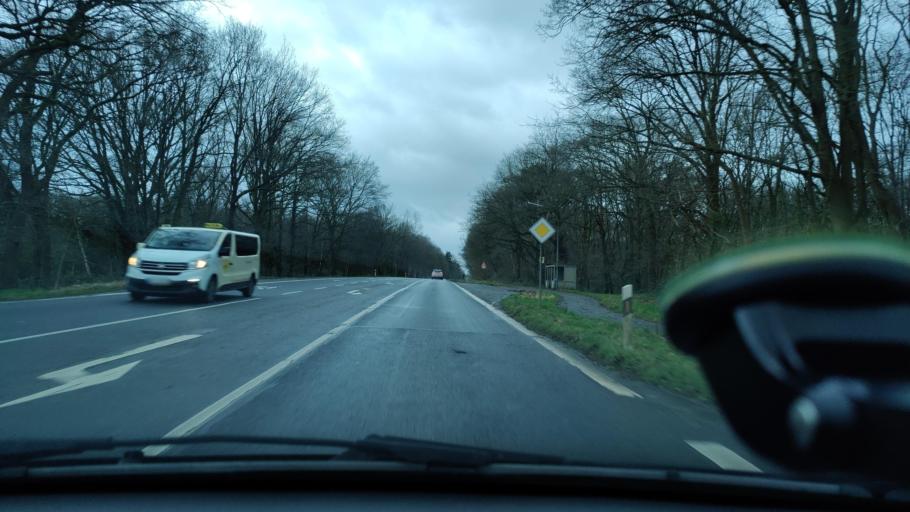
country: DE
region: North Rhine-Westphalia
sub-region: Regierungsbezirk Dusseldorf
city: Weeze
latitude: 51.6116
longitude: 6.1737
